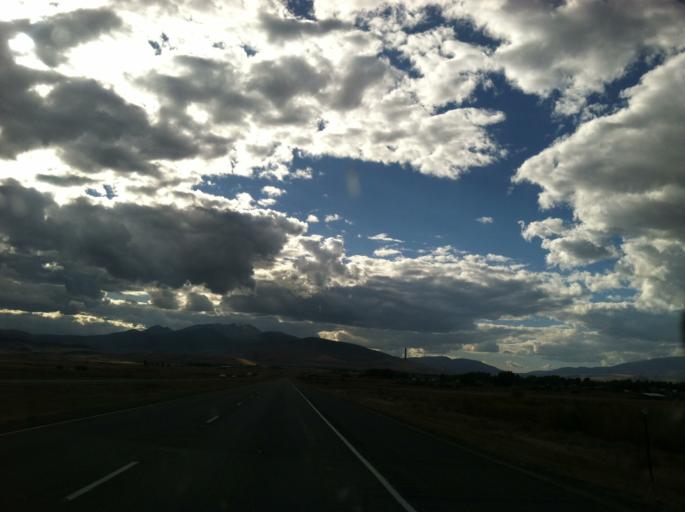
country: US
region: Montana
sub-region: Deer Lodge County
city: Warm Springs
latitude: 46.0957
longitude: -112.8111
